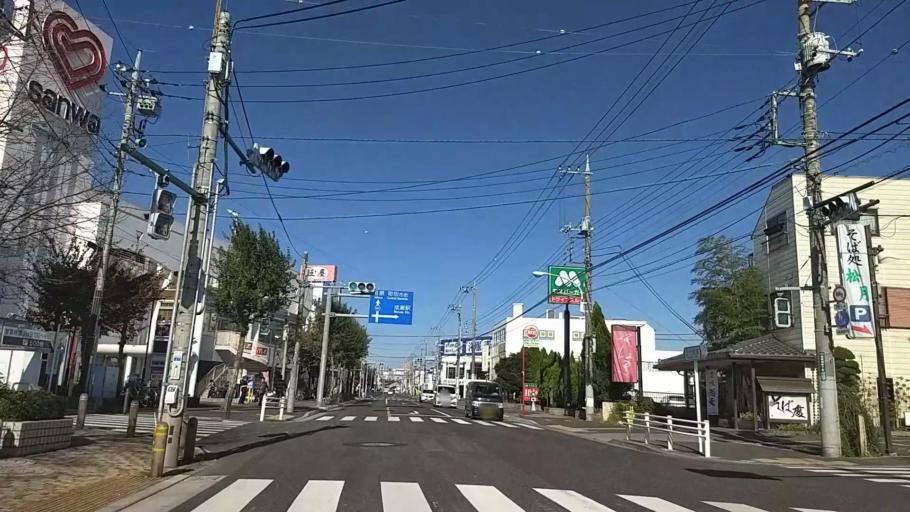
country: JP
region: Tokyo
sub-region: Machida-shi
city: Machida
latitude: 35.5258
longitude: 139.4661
